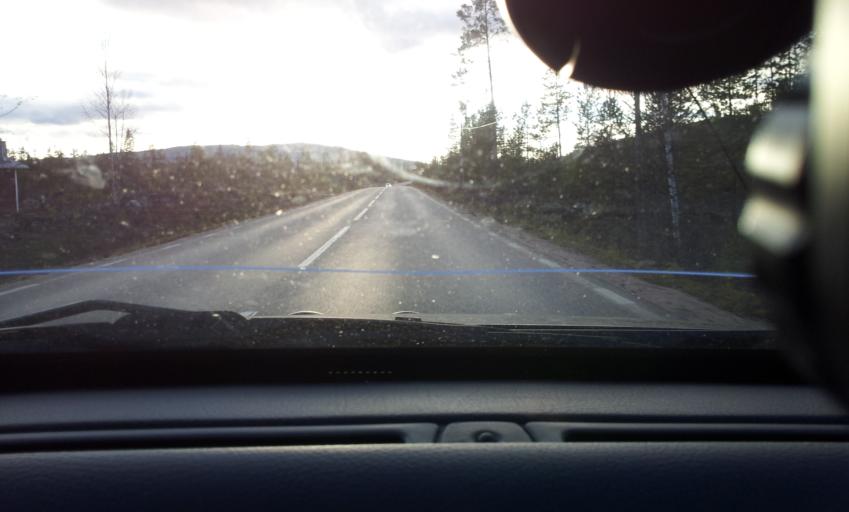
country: SE
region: Jaemtland
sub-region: Harjedalens Kommun
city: Sveg
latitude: 62.1243
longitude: 14.9970
